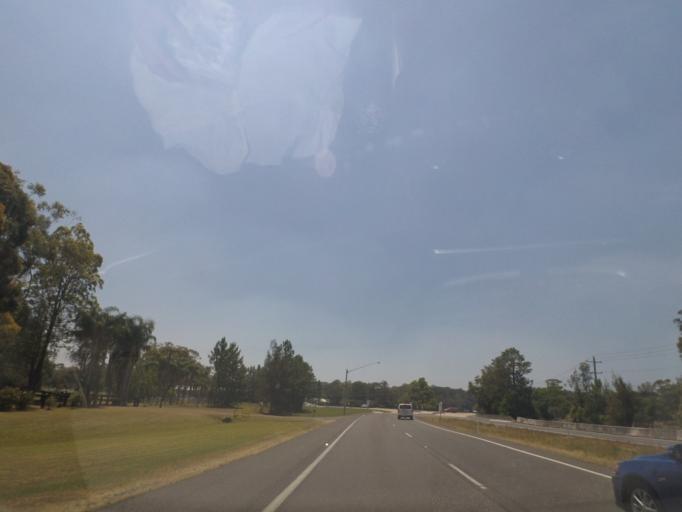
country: AU
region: New South Wales
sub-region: Port Stephens Shire
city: Medowie
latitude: -32.7901
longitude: 151.9016
